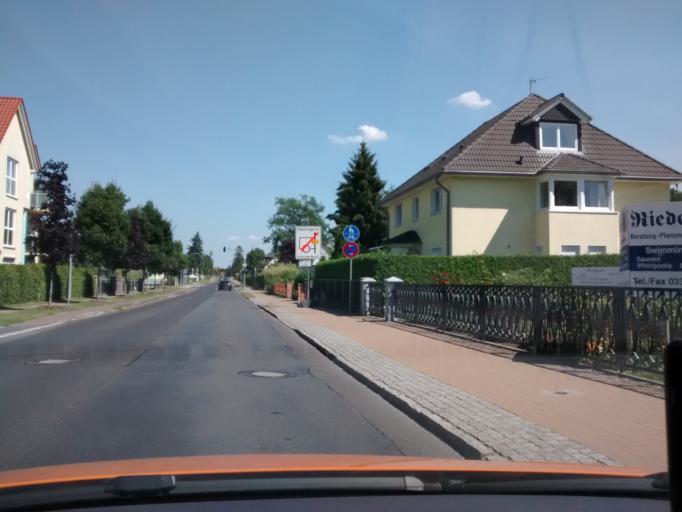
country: DE
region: Brandenburg
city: Hohen Neuendorf
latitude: 52.6663
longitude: 13.2720
